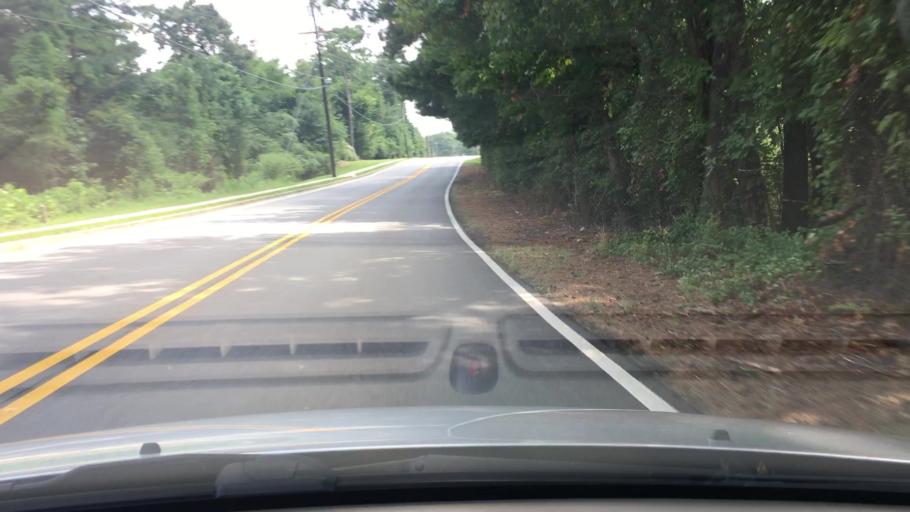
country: US
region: Georgia
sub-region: Fulton County
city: Alpharetta
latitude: 34.0584
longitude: -84.2753
